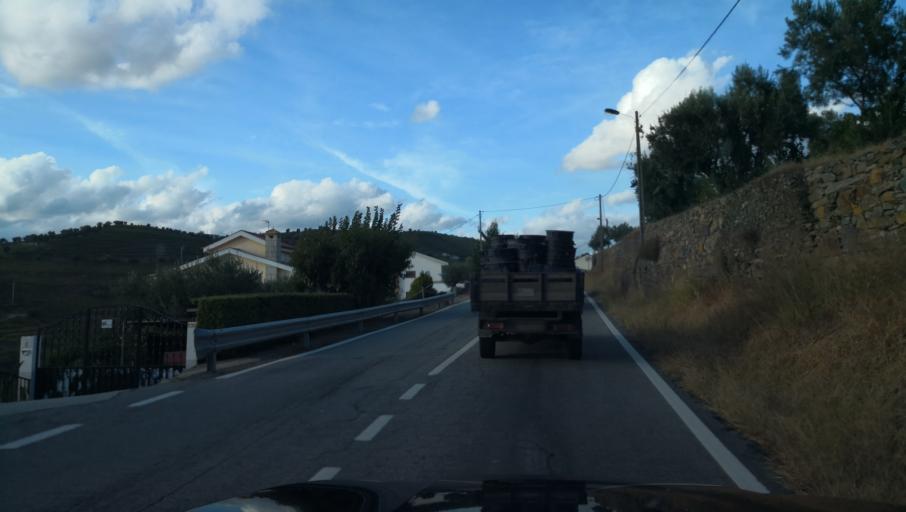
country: PT
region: Vila Real
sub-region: Peso da Regua
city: Peso da Regua
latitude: 41.1778
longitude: -7.7765
